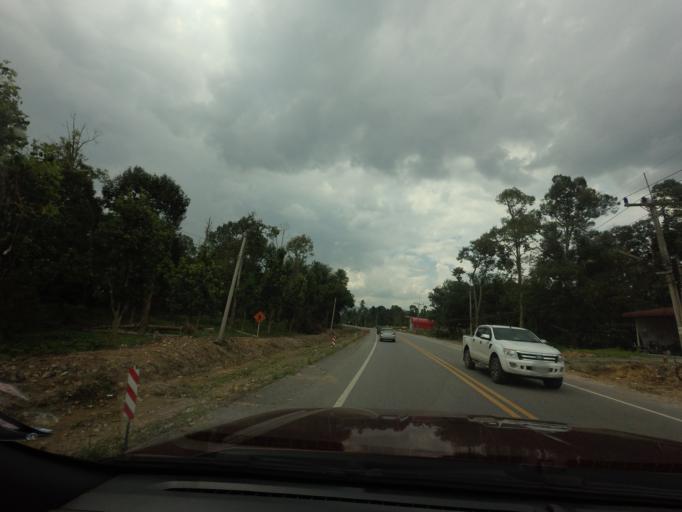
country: TH
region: Yala
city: Ban Nang Sata
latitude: 6.2988
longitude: 101.3015
